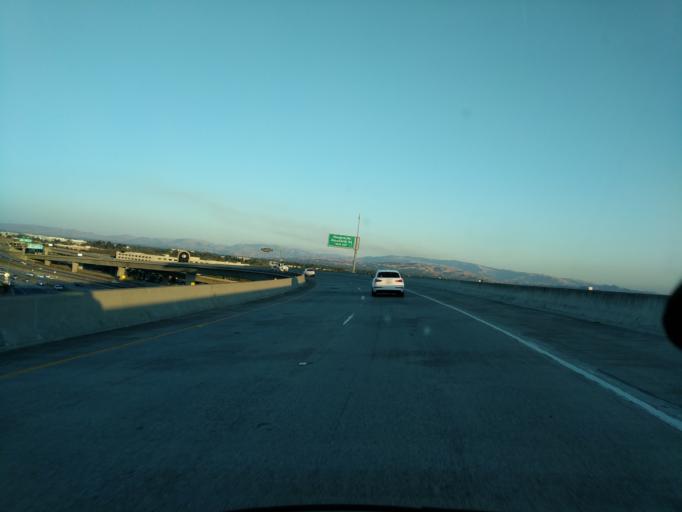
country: US
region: California
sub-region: Alameda County
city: Dublin
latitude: 37.7021
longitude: -121.9230
